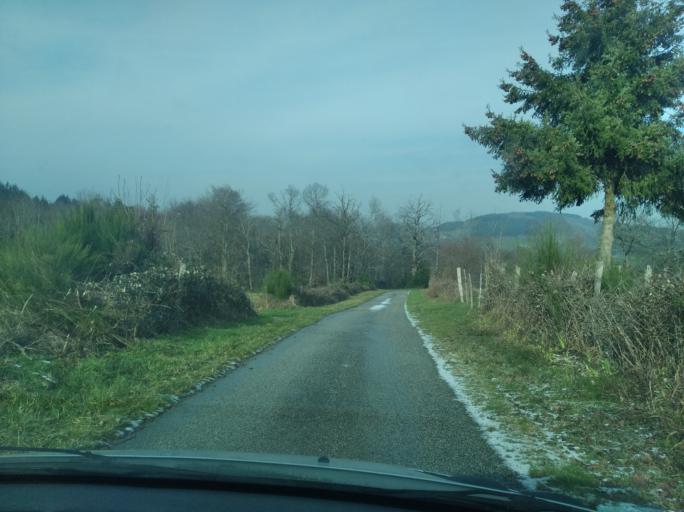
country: FR
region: Auvergne
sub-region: Departement de l'Allier
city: Le Mayet-de-Montagne
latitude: 46.1475
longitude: 3.7565
